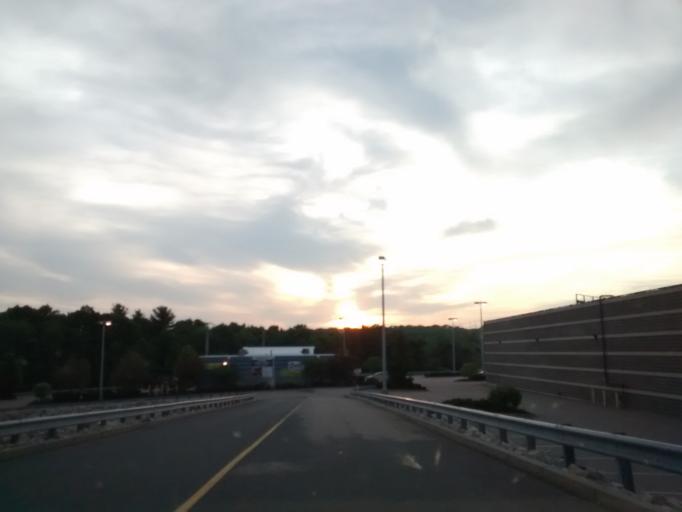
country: US
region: Massachusetts
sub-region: Worcester County
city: Milford
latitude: 42.1638
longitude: -71.5069
